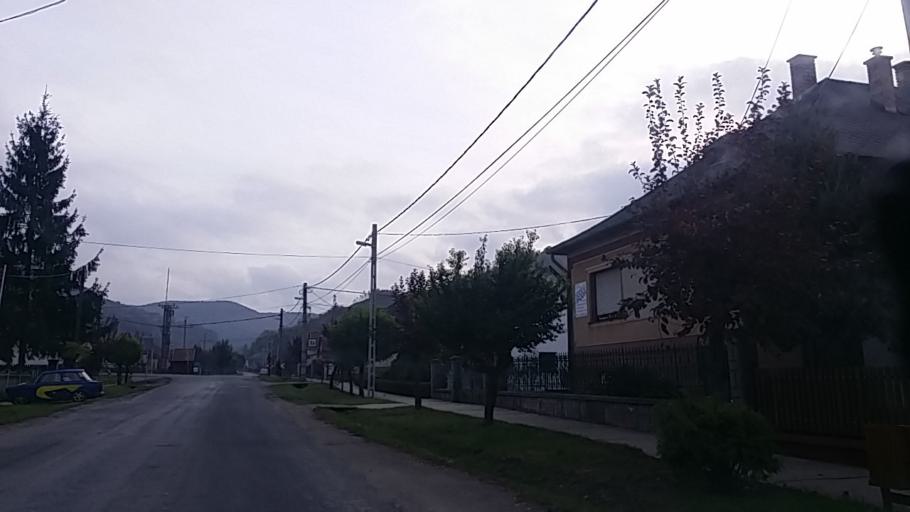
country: HU
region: Borsod-Abauj-Zemplen
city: Putnok
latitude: 48.2725
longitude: 20.4623
